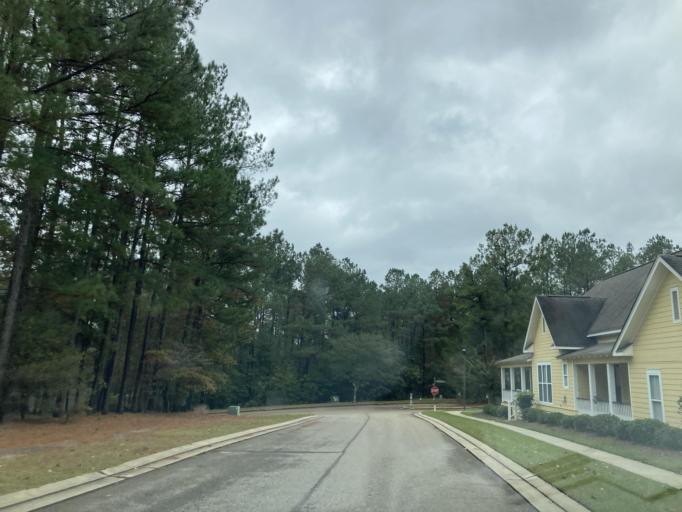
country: US
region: Mississippi
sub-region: Lamar County
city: West Hattiesburg
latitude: 31.2864
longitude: -89.4766
